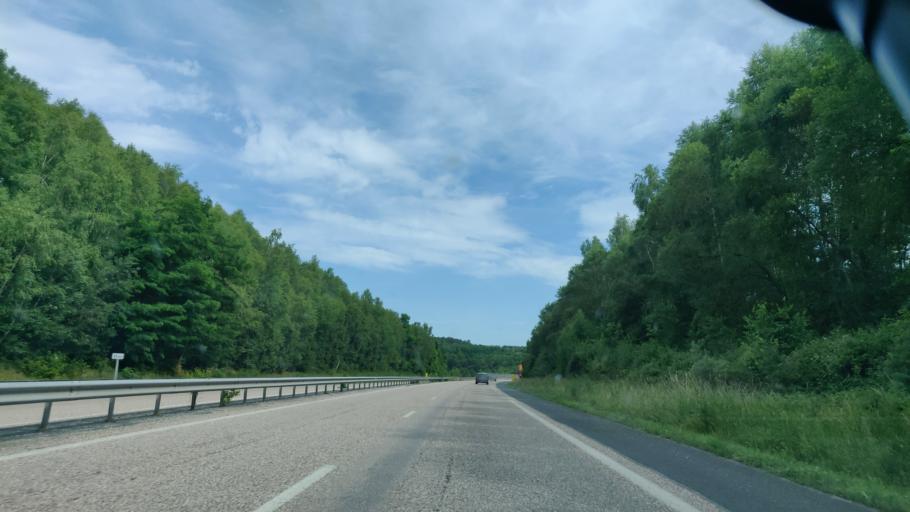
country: FR
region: Lorraine
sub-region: Departement de Meurthe-et-Moselle
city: Baccarat
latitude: 48.4637
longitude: 6.7438
